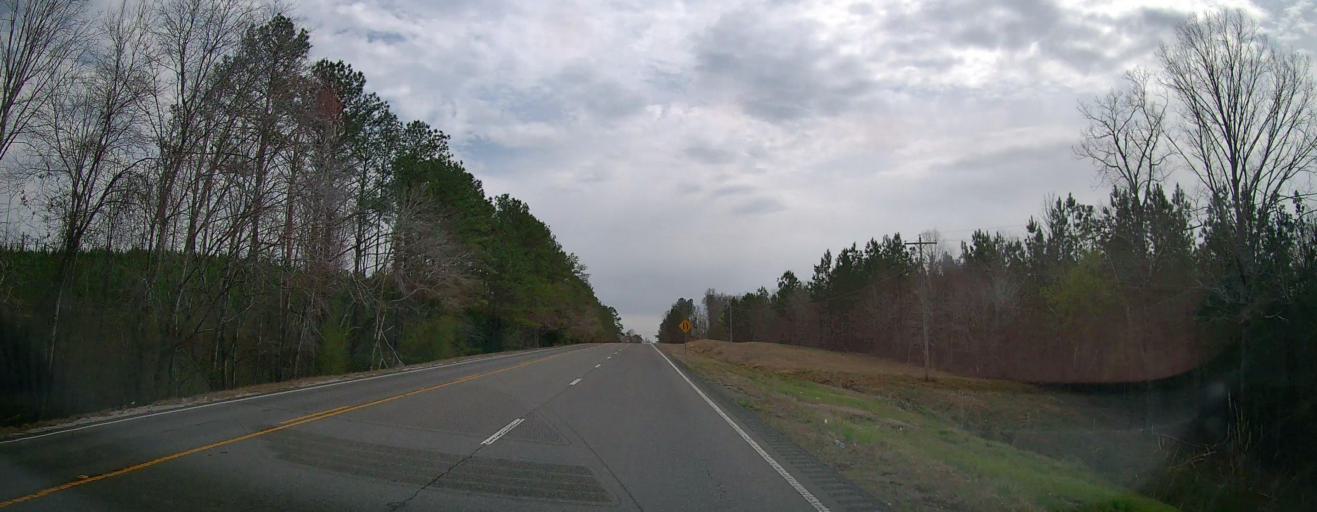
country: US
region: Alabama
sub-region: Marion County
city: Hamilton
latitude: 34.0580
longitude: -87.9673
